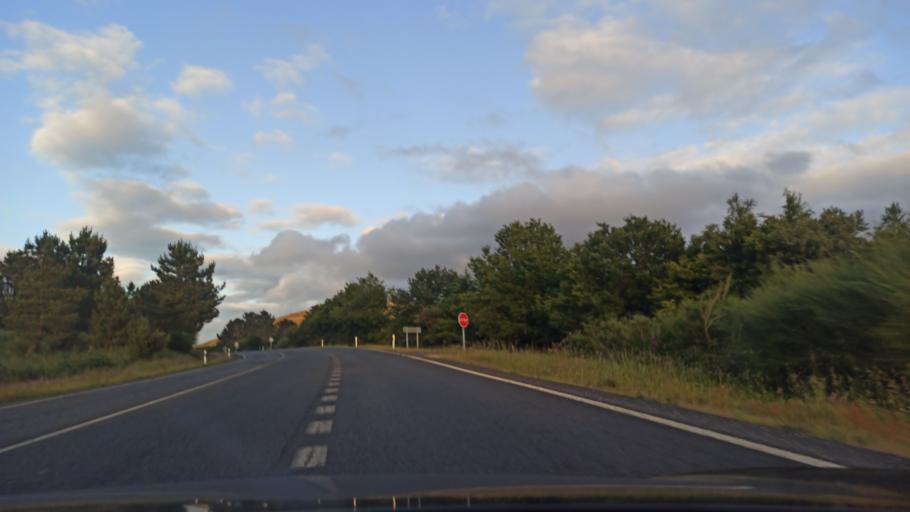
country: ES
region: Galicia
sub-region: Provincia de Pontevedra
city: Rodeiro
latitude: 42.7687
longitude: -7.9792
